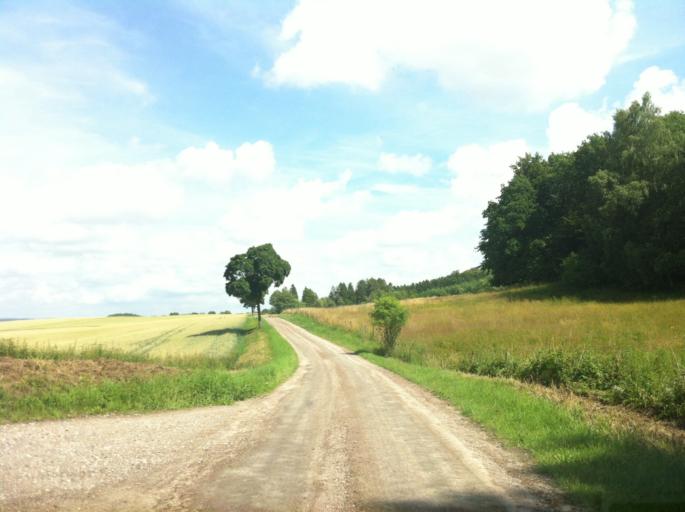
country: SE
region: Skane
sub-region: Trelleborgs Kommun
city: Anderslov
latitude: 55.4408
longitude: 13.3706
